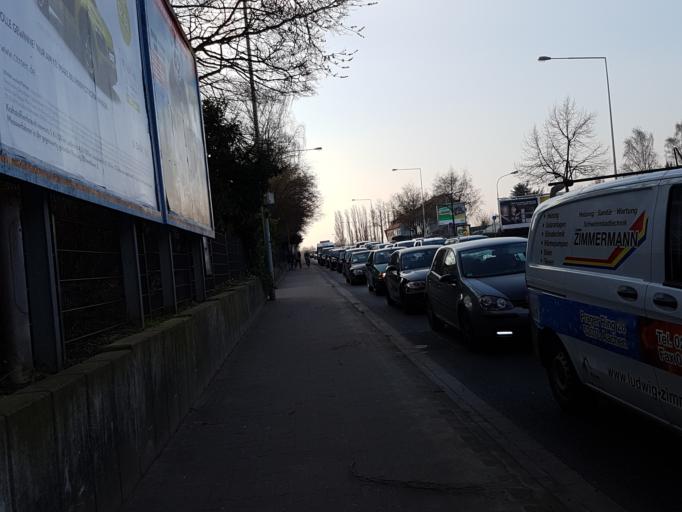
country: DE
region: North Rhine-Westphalia
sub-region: Regierungsbezirk Koln
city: Wurselen
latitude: 50.7930
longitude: 6.1162
